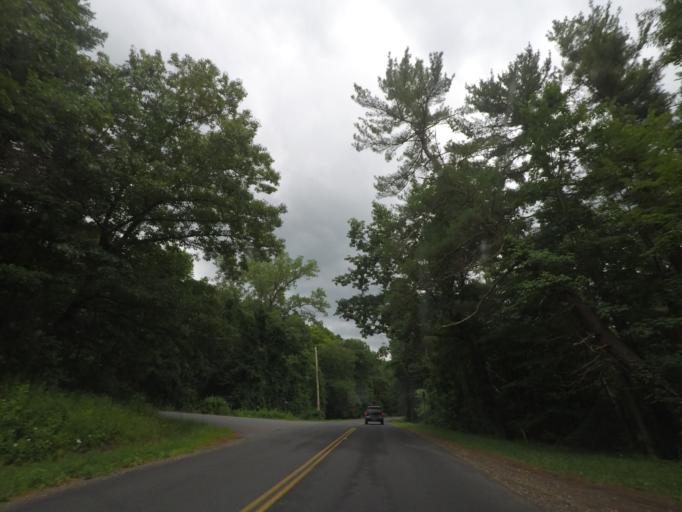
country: US
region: New York
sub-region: Rensselaer County
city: Poestenkill
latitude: 42.8248
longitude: -73.5175
